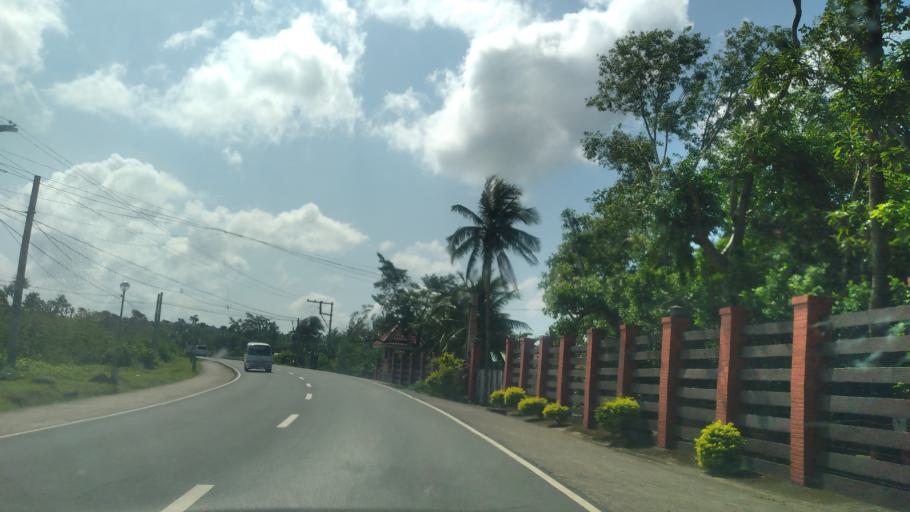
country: PH
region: Calabarzon
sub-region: Province of Quezon
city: Unisan
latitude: 13.8351
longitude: 121.9787
